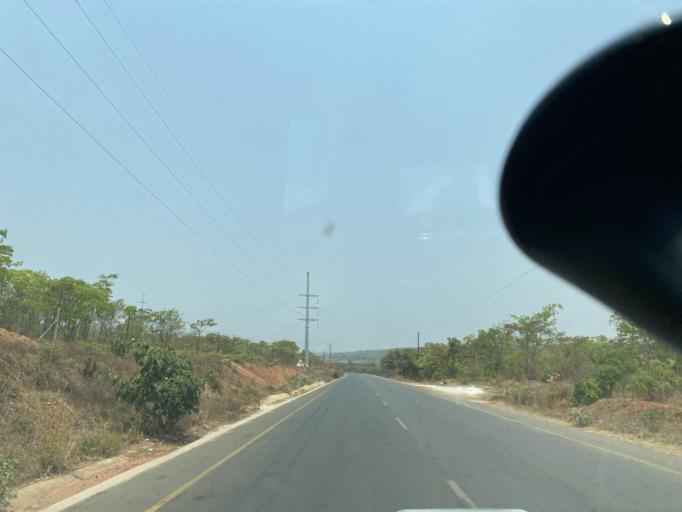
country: ZM
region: Lusaka
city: Lusaka
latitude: -15.5406
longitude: 28.4732
